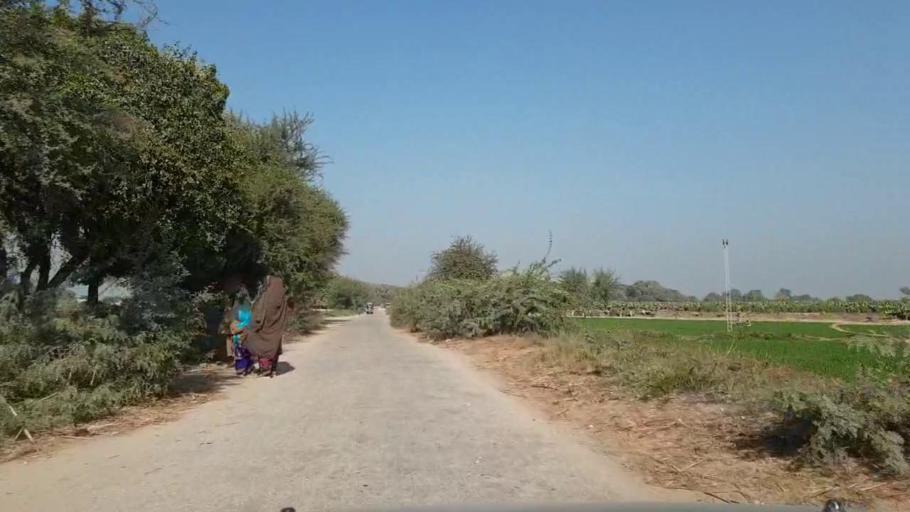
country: PK
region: Sindh
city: Matiari
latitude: 25.5843
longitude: 68.6019
